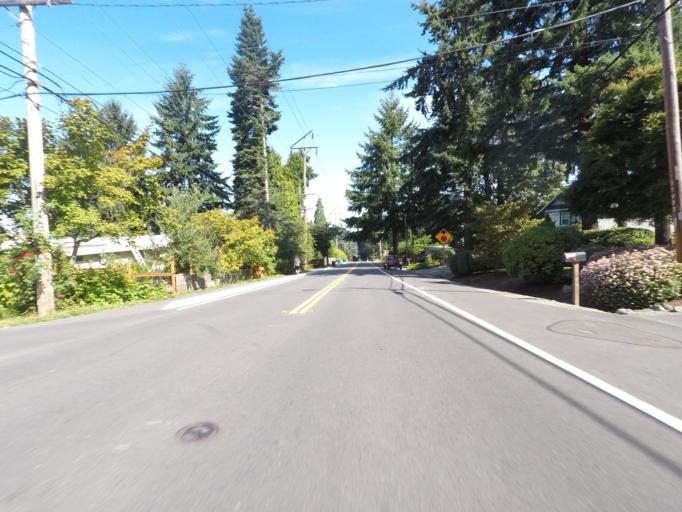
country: US
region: Washington
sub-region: King County
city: Kenmore
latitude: 47.7435
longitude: -122.2288
